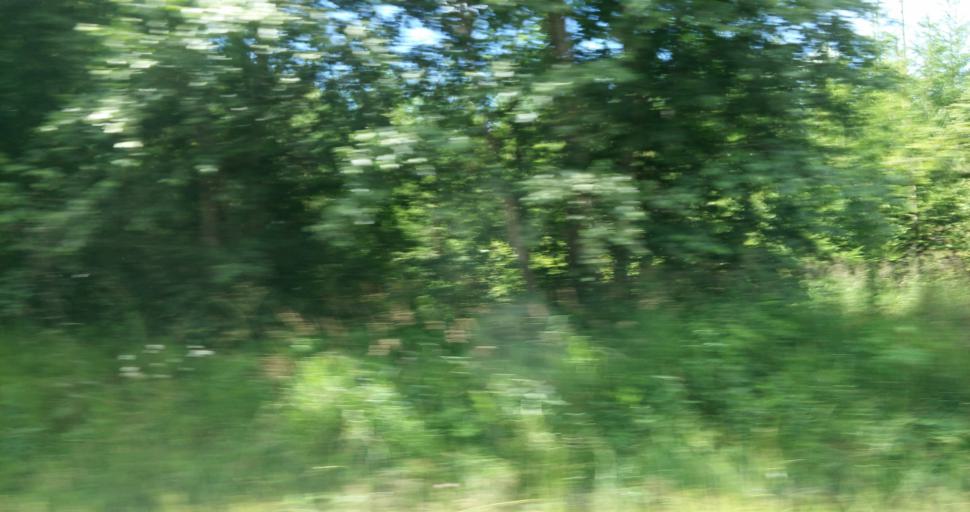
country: SE
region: Vaermland
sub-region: Hagfors Kommun
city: Ekshaerad
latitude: 60.0802
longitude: 13.4544
